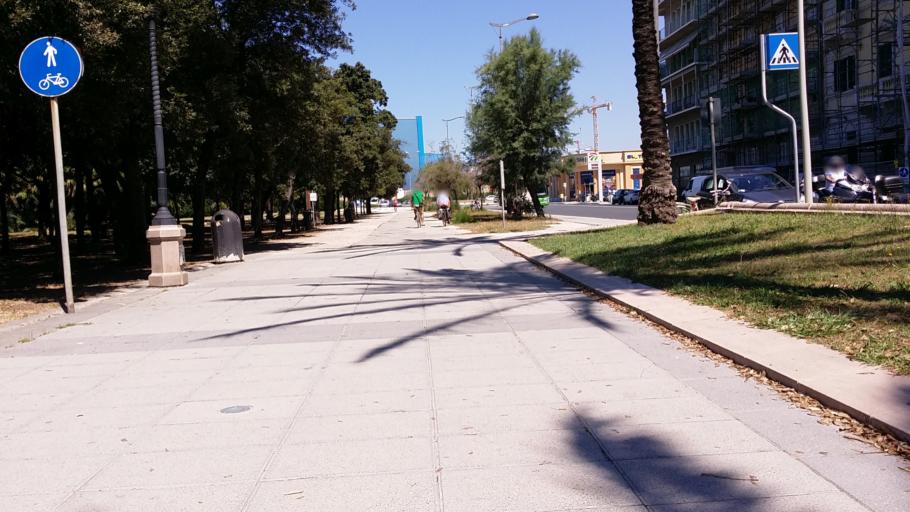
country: IT
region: Tuscany
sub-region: Provincia di Livorno
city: Livorno
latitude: 43.5396
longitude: 10.3018
